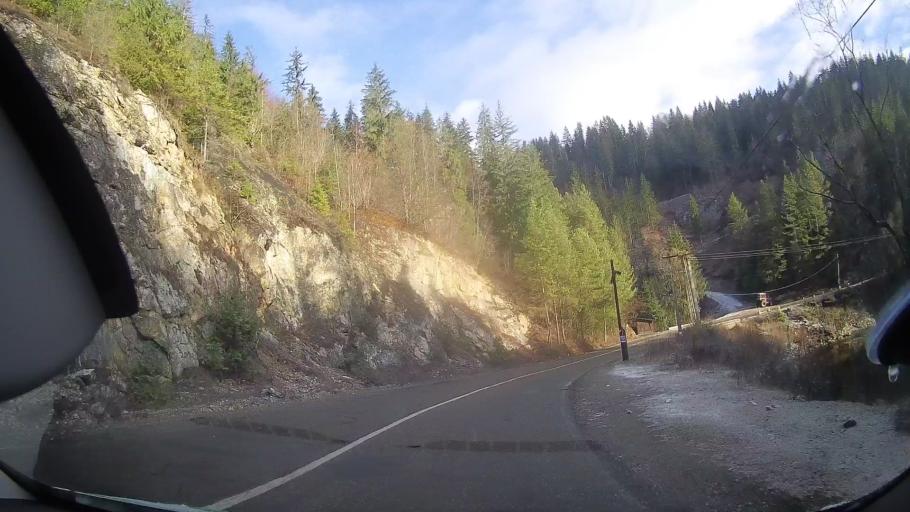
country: RO
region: Alba
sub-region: Comuna Albac
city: Albac
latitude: 46.4563
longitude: 22.9260
